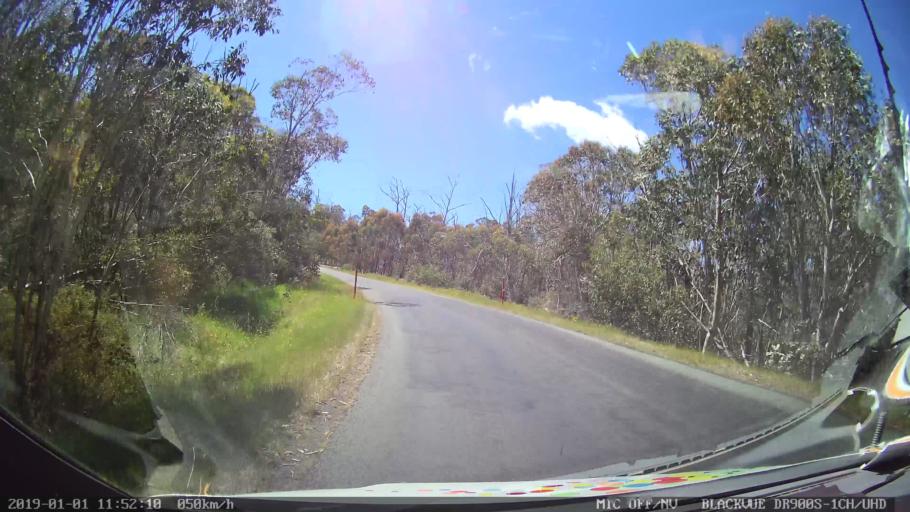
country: AU
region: New South Wales
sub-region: Snowy River
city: Jindabyne
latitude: -35.8880
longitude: 148.4329
